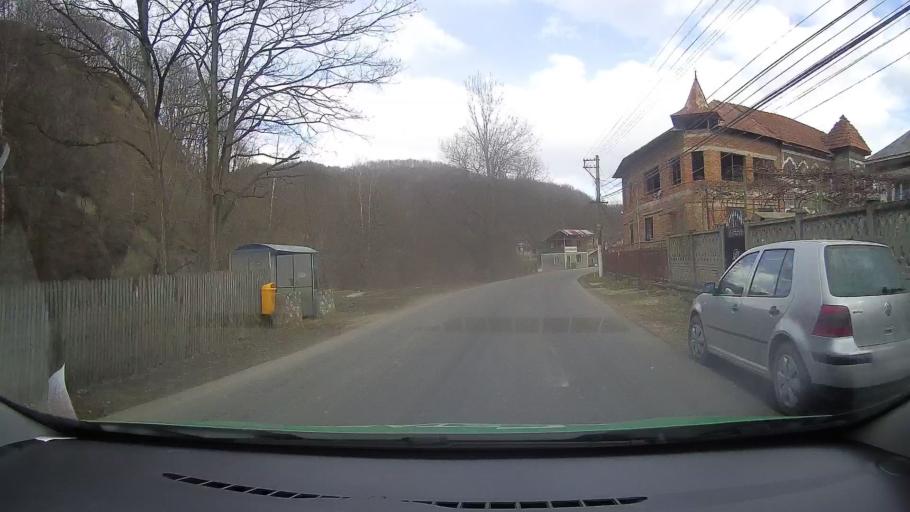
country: RO
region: Dambovita
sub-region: Comuna Visinesti
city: Visinesti
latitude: 45.1092
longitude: 25.5516
